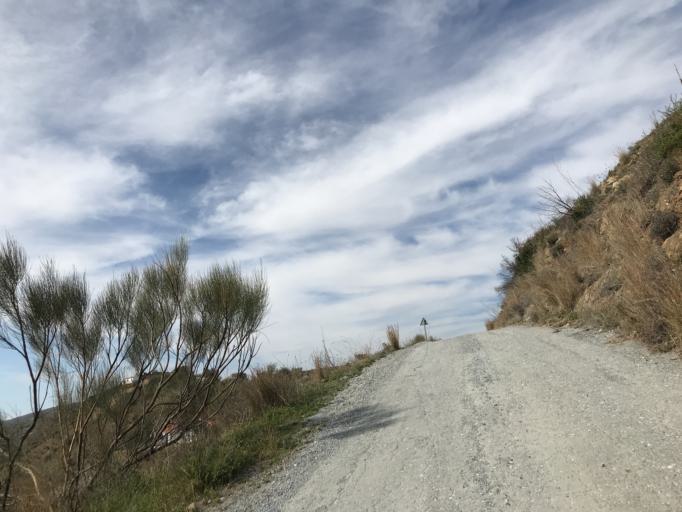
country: ES
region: Andalusia
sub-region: Provincia de Malaga
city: Almachar
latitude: 36.7822
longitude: -4.2199
